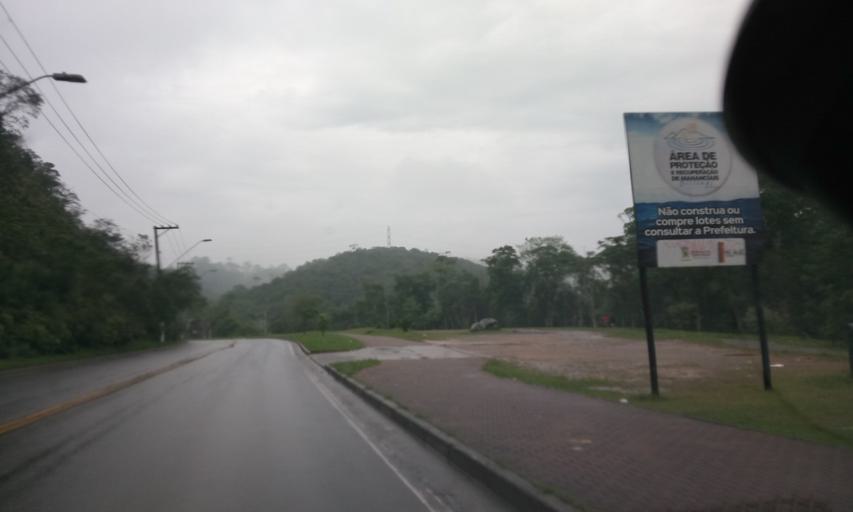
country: BR
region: Sao Paulo
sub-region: Maua
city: Maua
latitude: -23.7278
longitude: -46.4955
